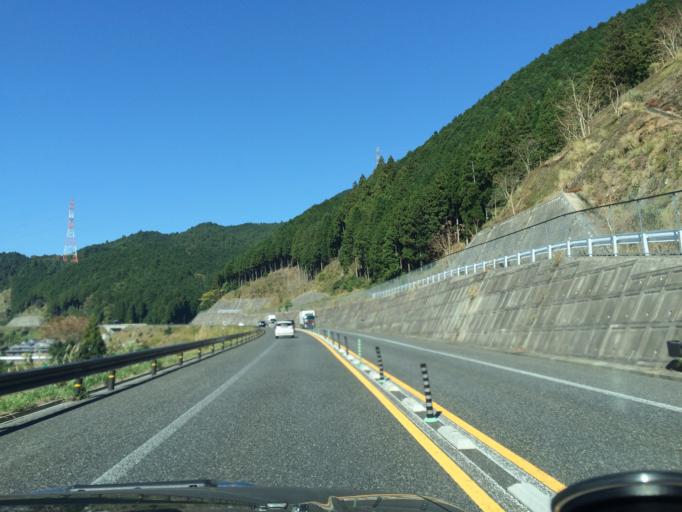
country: JP
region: Kyoto
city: Fukuchiyama
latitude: 35.2822
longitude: 134.9858
